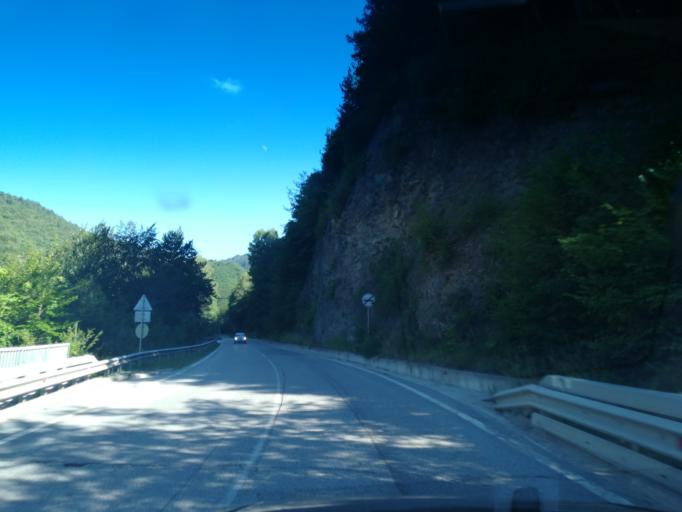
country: BG
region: Smolyan
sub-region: Obshtina Chepelare
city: Chepelare
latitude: 41.8133
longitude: 24.7030
